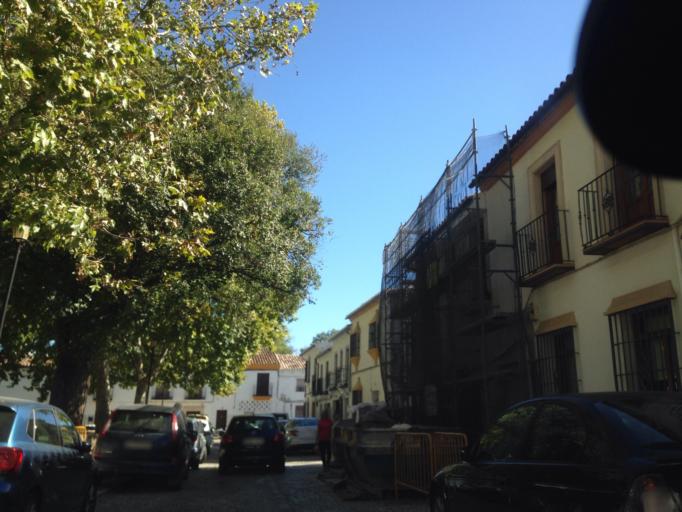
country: ES
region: Andalusia
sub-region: Provincia de Malaga
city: Ronda
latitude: 36.7335
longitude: -5.1649
